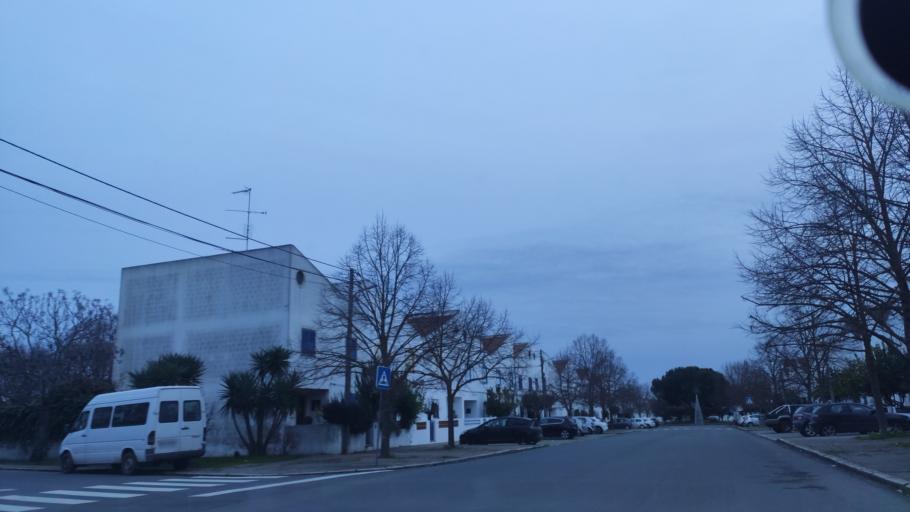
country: PT
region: Beja
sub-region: Beja
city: Beja
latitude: 38.0192
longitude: -7.8516
